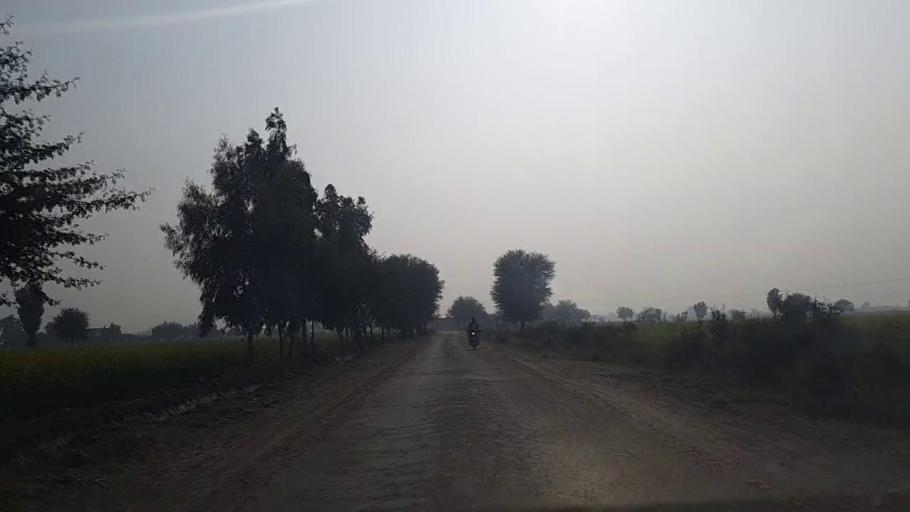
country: PK
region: Sindh
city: Sanghar
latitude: 26.0871
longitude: 68.8774
